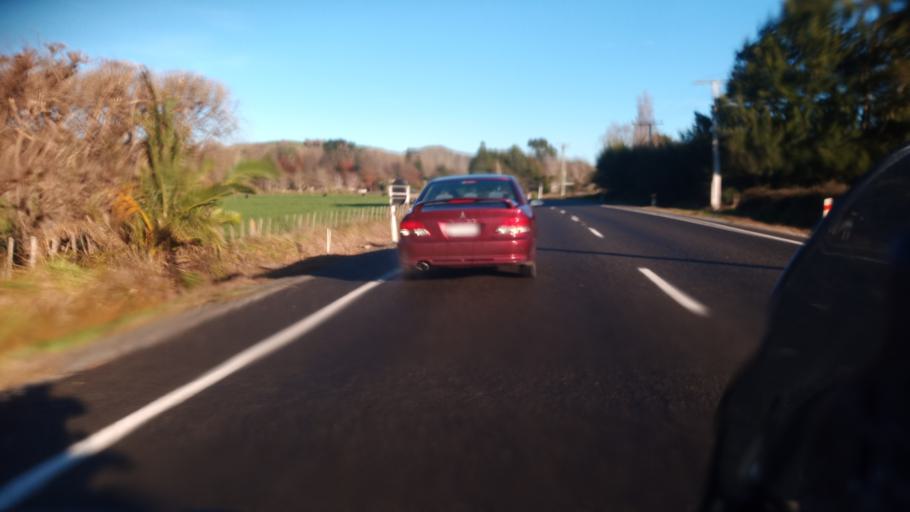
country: NZ
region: Hawke's Bay
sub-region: Wairoa District
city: Wairoa
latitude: -39.0384
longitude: 177.4074
